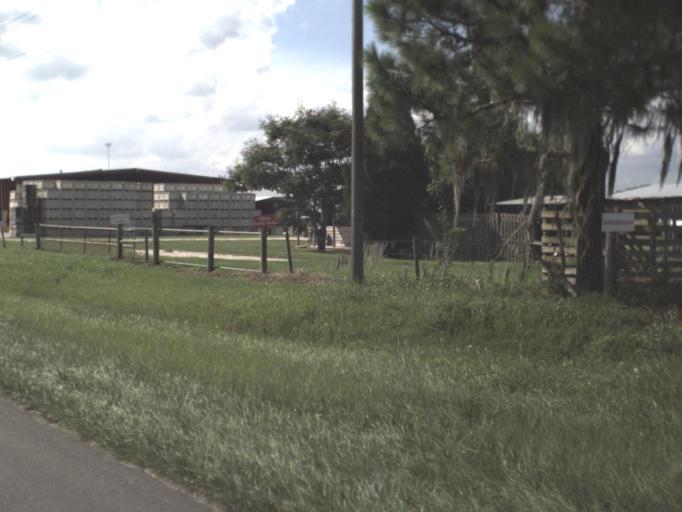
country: US
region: Florida
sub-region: Sarasota County
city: The Meadows
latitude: 27.4755
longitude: -82.3724
